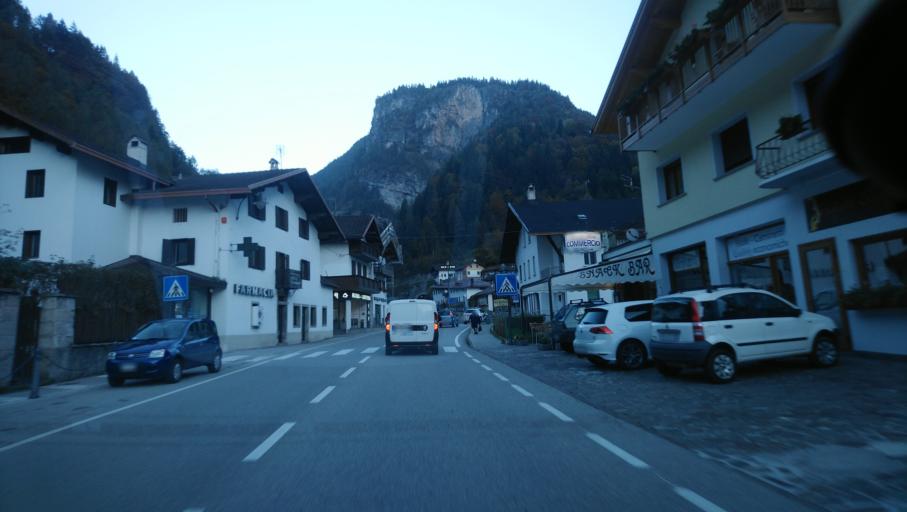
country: IT
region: Veneto
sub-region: Provincia di Belluno
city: Cencenighe Agordino
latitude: 46.3513
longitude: 11.9669
